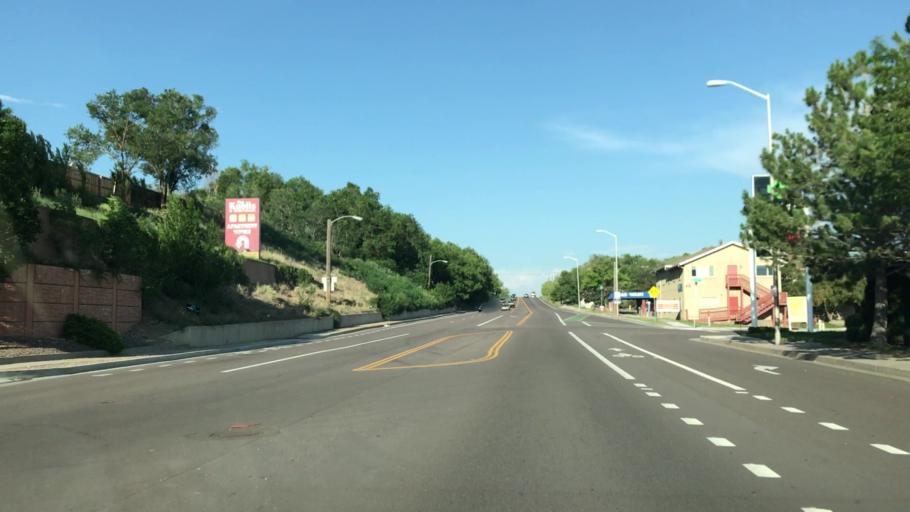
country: US
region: Colorado
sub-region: El Paso County
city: Colorado Springs
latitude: 38.8480
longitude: -104.8465
